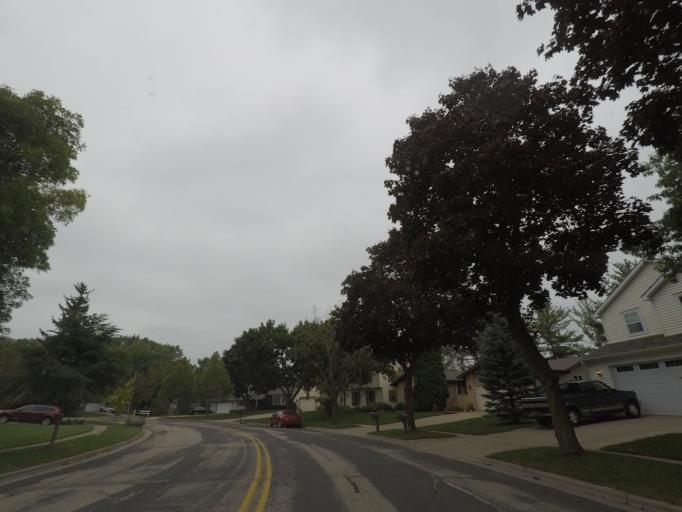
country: US
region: Wisconsin
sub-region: Dane County
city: Middleton
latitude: 43.0876
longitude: -89.5138
